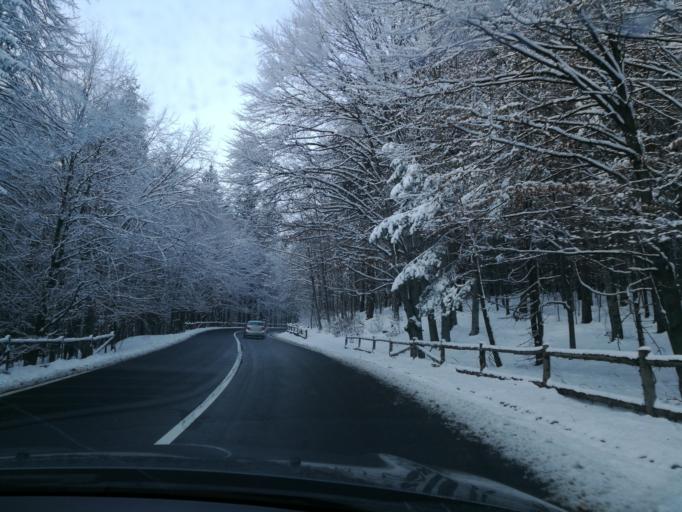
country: RO
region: Brasov
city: Brasov
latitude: 45.6171
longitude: 25.5463
